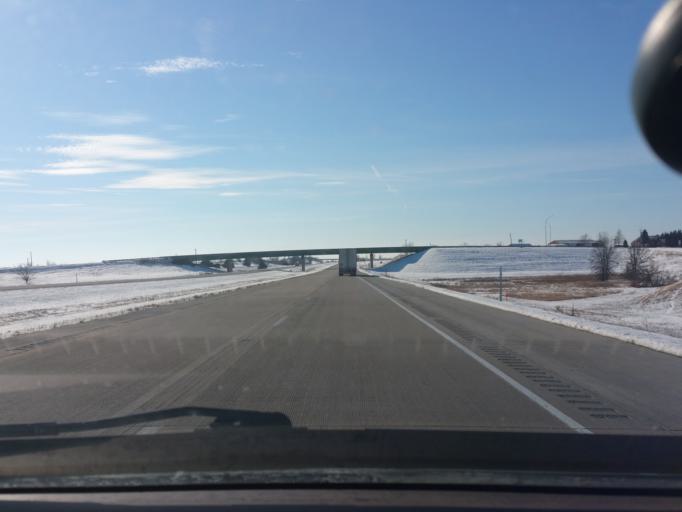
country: US
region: Iowa
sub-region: Decatur County
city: Leon
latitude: 40.8145
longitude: -93.8262
